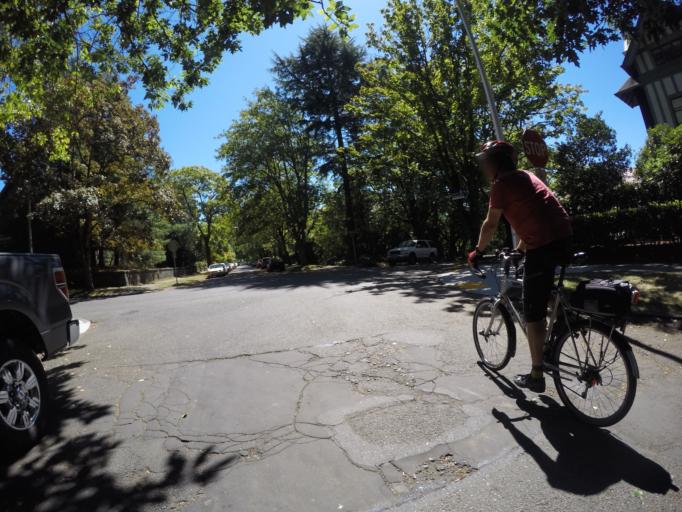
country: US
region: Washington
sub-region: King County
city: Seattle
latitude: 47.6271
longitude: -122.3146
